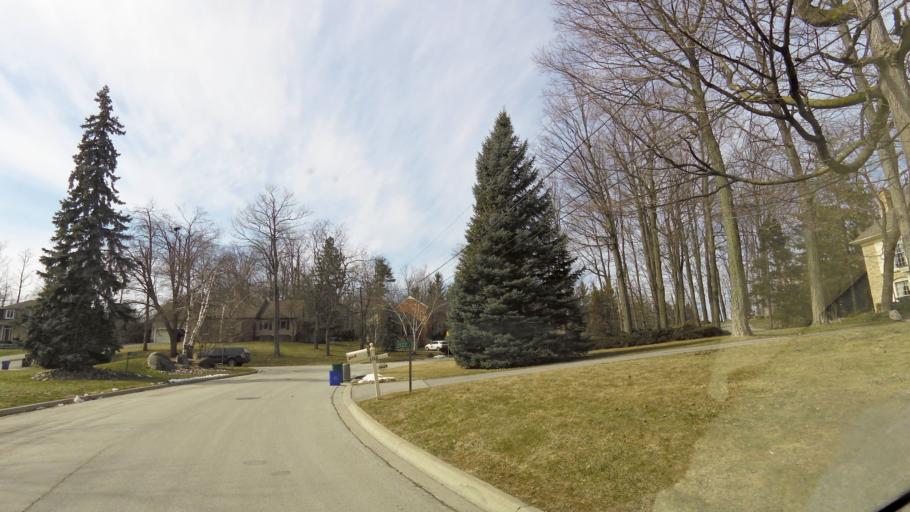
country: CA
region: Ontario
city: Burlington
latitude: 43.3711
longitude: -79.8602
